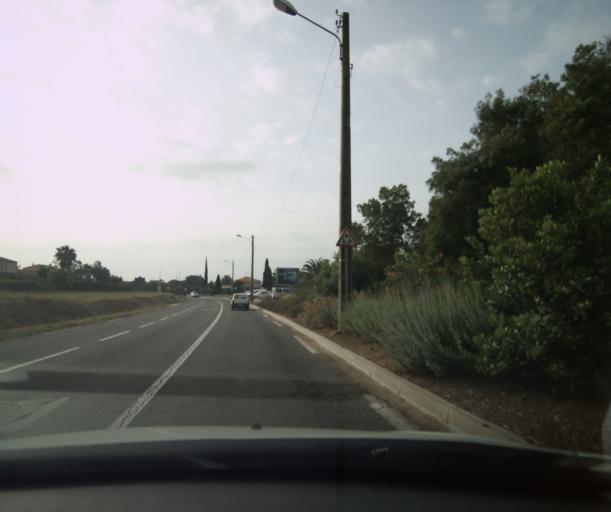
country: FR
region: Provence-Alpes-Cote d'Azur
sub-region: Departement du Var
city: Hyeres
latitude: 43.1171
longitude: 6.1453
